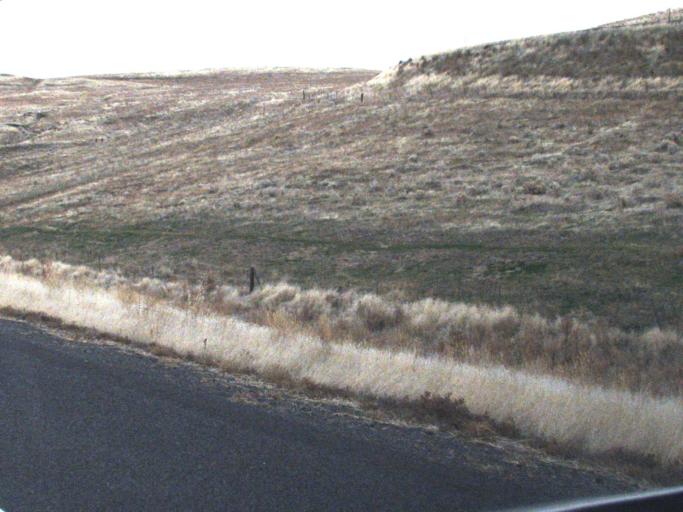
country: US
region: Washington
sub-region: Adams County
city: Ritzville
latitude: 46.7793
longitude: -118.0859
